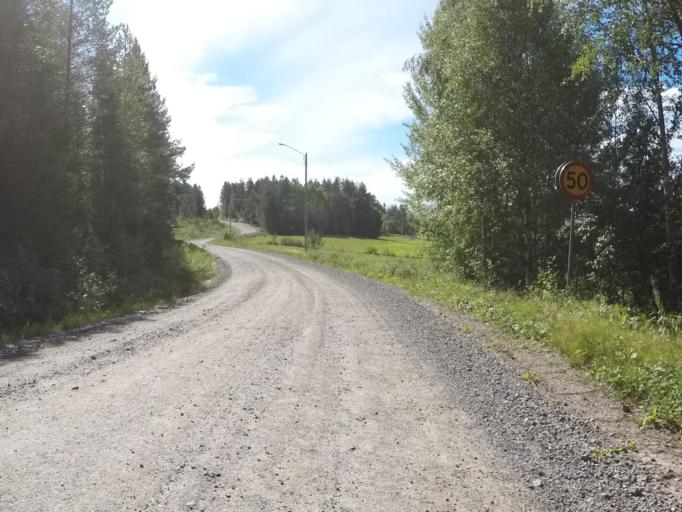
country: SE
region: Vaesterbotten
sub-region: Robertsfors Kommun
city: Robertsfors
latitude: 64.0049
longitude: 20.8134
